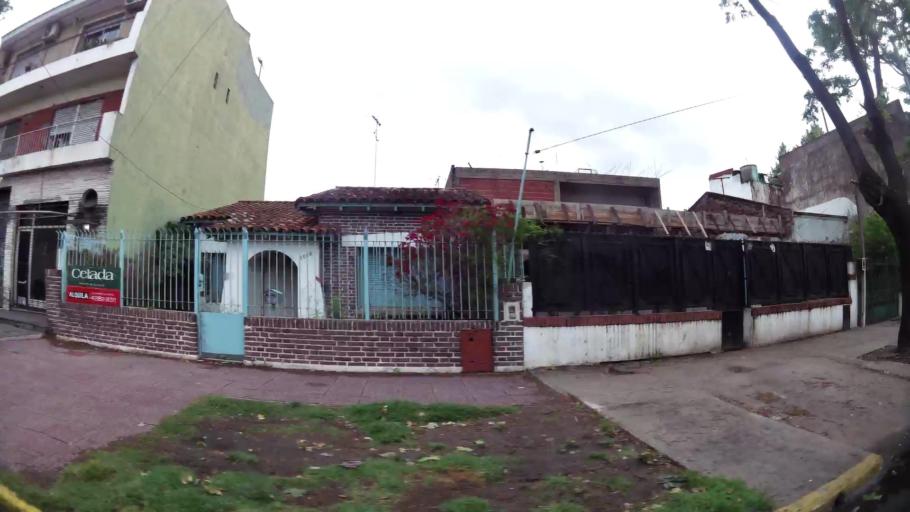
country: AR
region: Buenos Aires
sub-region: Partido de Lomas de Zamora
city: Lomas de Zamora
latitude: -34.7593
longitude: -58.3825
